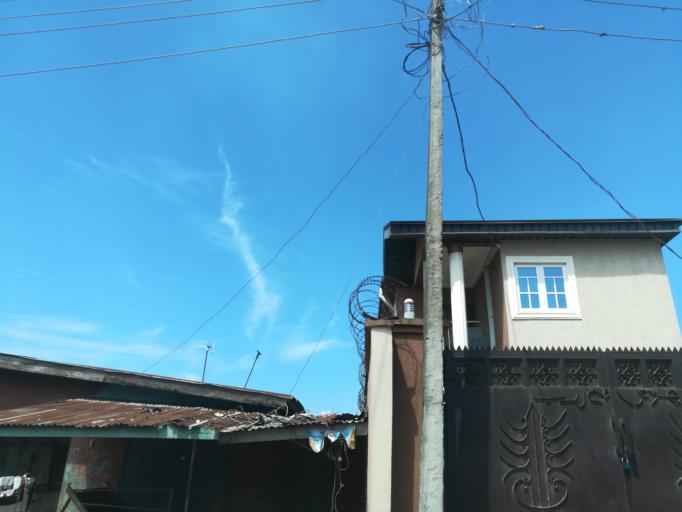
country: NG
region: Lagos
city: Oshodi
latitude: 6.5621
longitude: 3.3315
